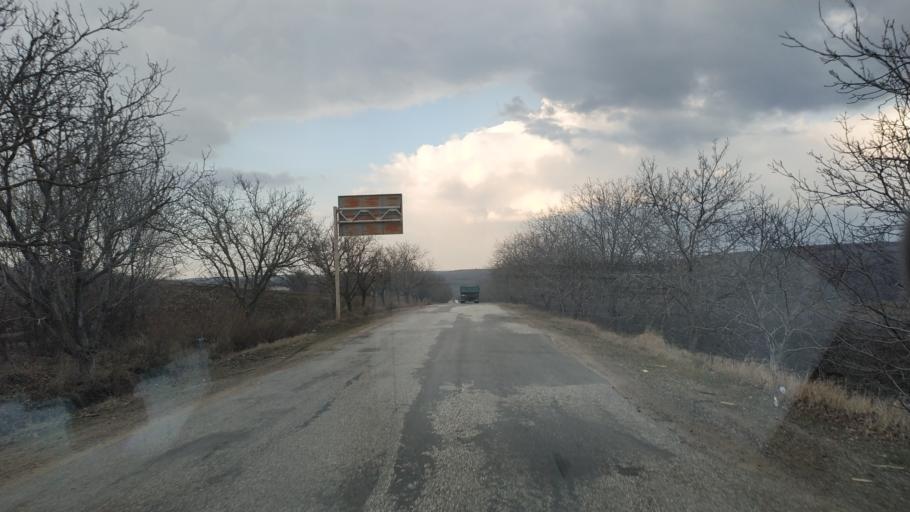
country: MD
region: Anenii Noi
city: Anenii Noi
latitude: 46.9337
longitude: 29.2862
